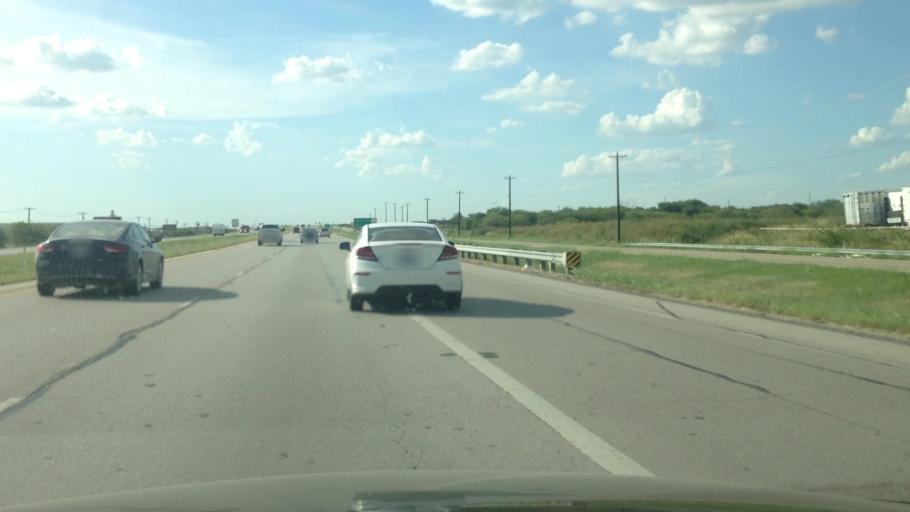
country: US
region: Texas
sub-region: Tarrant County
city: Haslet
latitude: 32.9194
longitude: -97.3520
